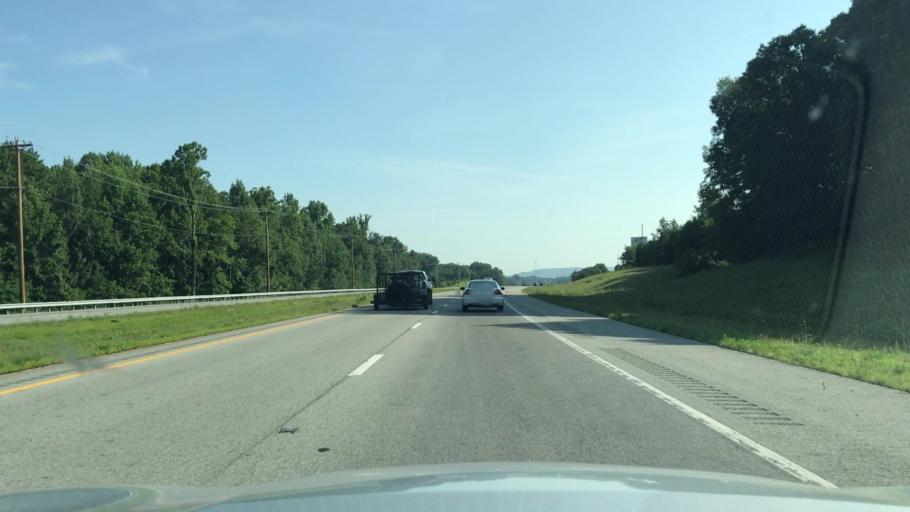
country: US
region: Tennessee
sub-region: Overton County
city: Livingston
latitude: 36.3216
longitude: -85.3616
